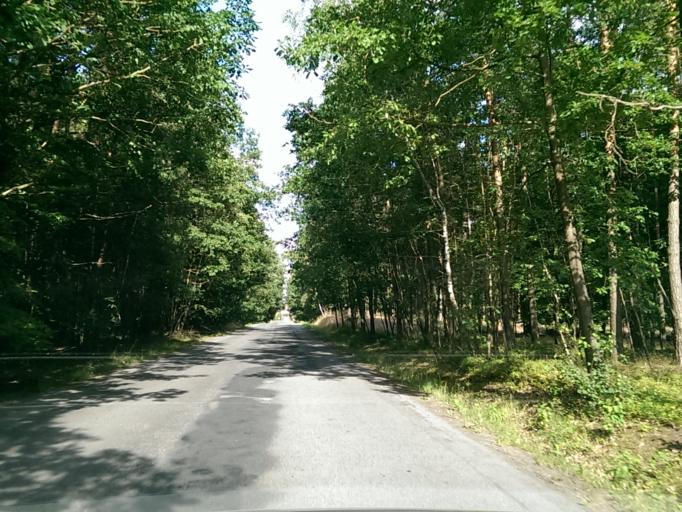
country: CZ
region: Central Bohemia
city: Bakov nad Jizerou
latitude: 50.4756
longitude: 14.8790
